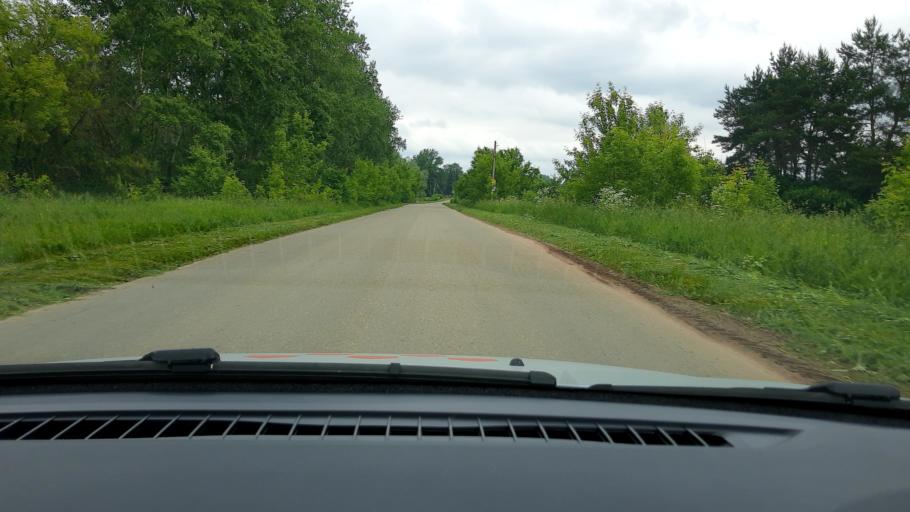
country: RU
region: Nizjnij Novgorod
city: Bogorodsk
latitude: 56.0690
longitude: 43.5039
